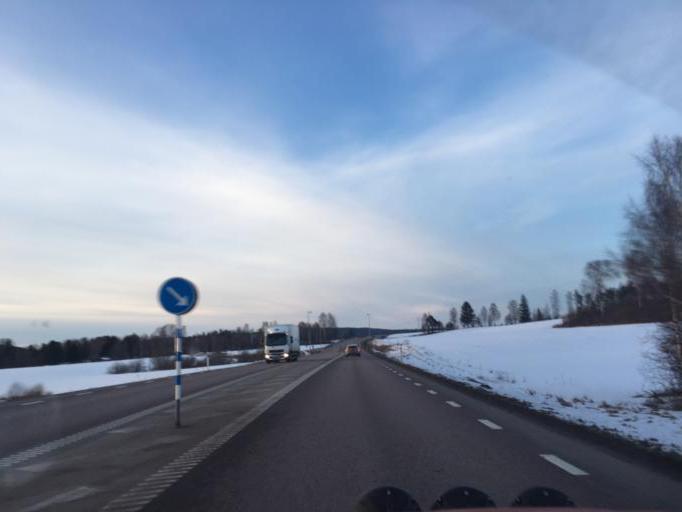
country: SE
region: Dalarna
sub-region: Gagnefs Kommun
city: Gagnef
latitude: 60.6078
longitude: 15.0509
